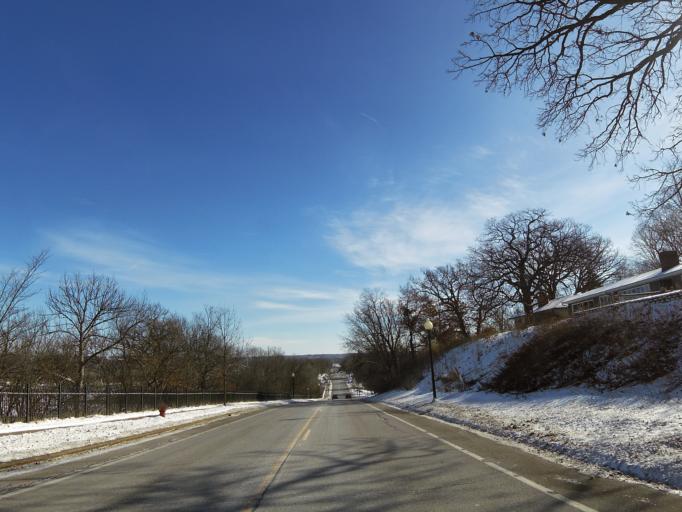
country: US
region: Minnesota
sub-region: Dakota County
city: Hastings
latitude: 44.7443
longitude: -92.8619
